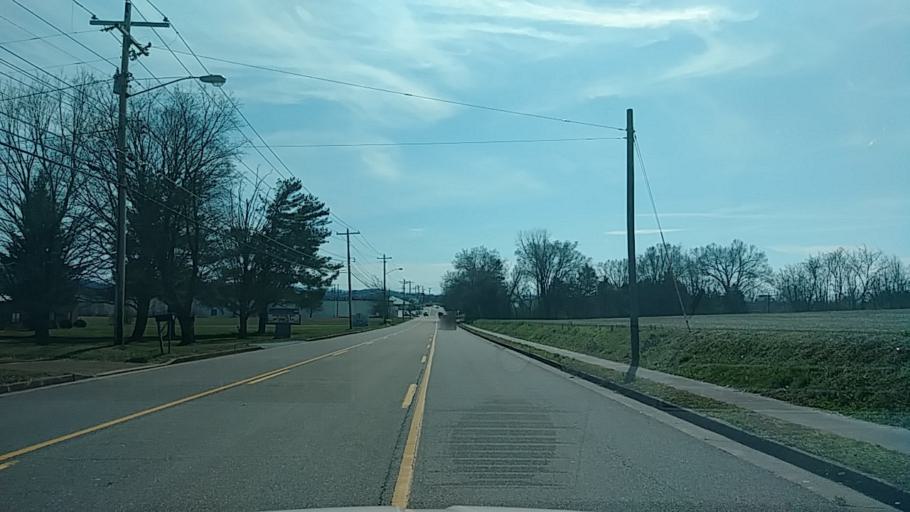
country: US
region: Tennessee
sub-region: Hamblen County
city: Morristown
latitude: 36.2050
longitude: -83.3348
